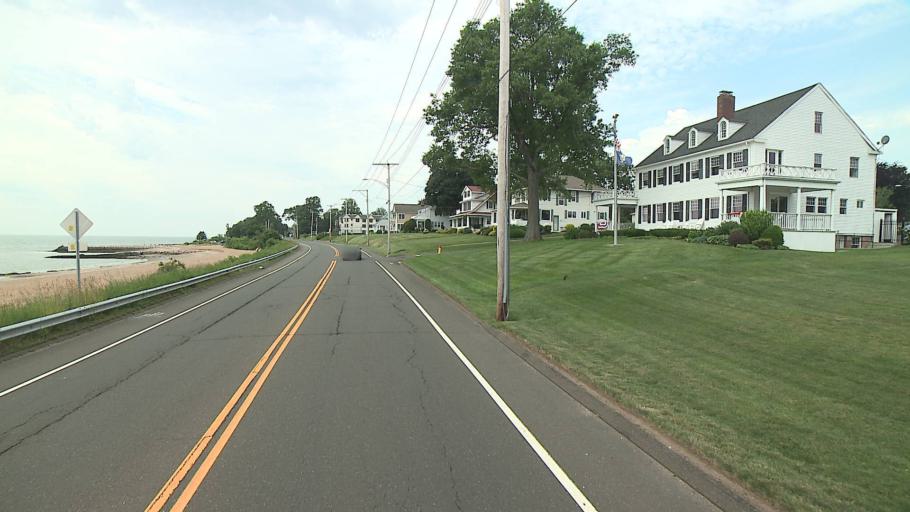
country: US
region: Connecticut
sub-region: New Haven County
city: Woodmont
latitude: 41.2434
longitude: -72.9701
